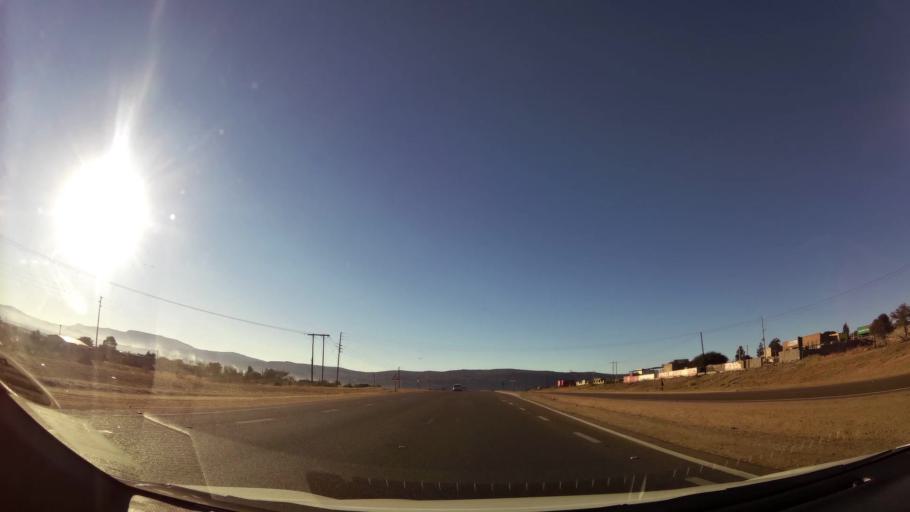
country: ZA
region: Limpopo
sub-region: Capricorn District Municipality
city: Mankoeng
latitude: -23.9088
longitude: 29.7704
